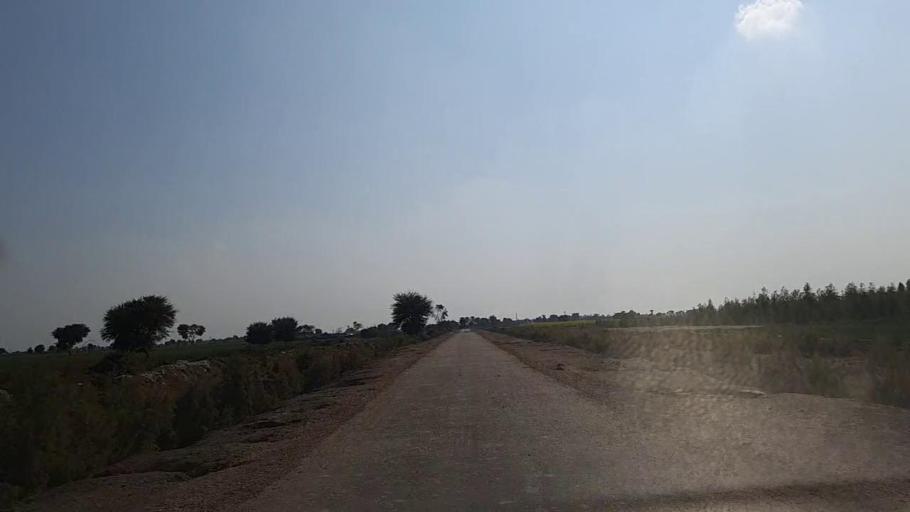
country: PK
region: Sindh
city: Jam Sahib
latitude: 26.2486
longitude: 68.5668
